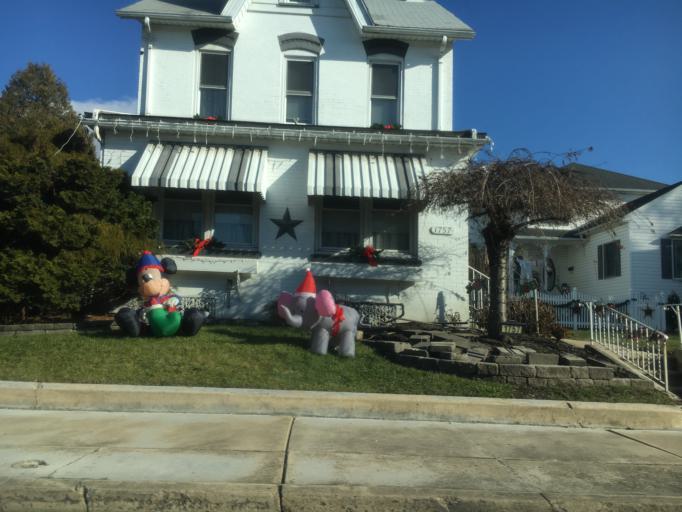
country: US
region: Pennsylvania
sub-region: Northampton County
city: Northampton
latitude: 40.6871
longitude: -75.4975
